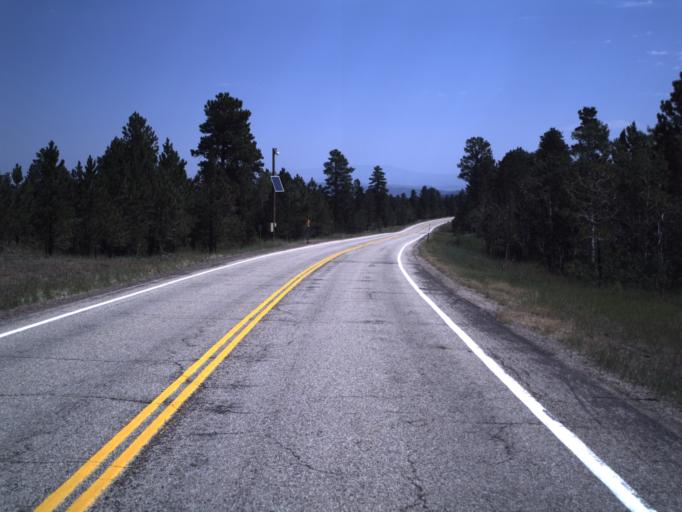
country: US
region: Utah
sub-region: Daggett County
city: Manila
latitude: 40.8471
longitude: -109.6418
